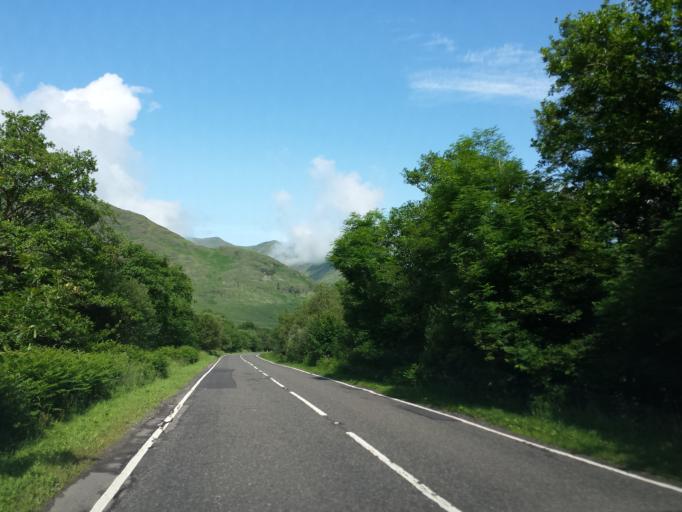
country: GB
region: Scotland
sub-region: Argyll and Bute
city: Garelochhead
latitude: 56.4060
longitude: -5.0138
